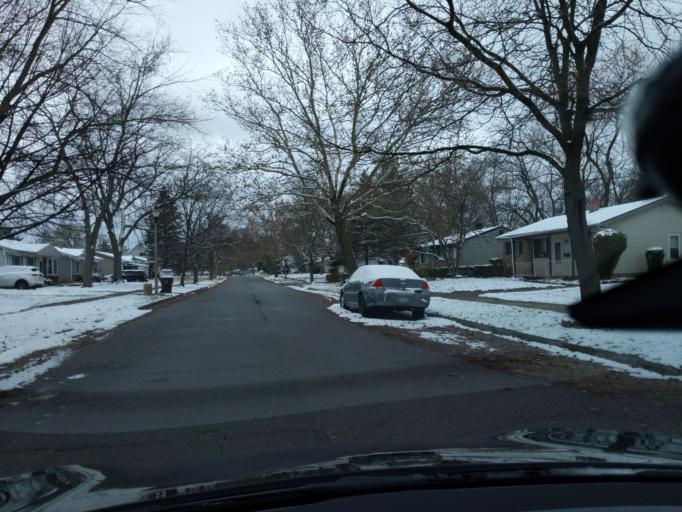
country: US
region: Michigan
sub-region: Eaton County
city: Waverly
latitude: 42.6871
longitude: -84.5961
